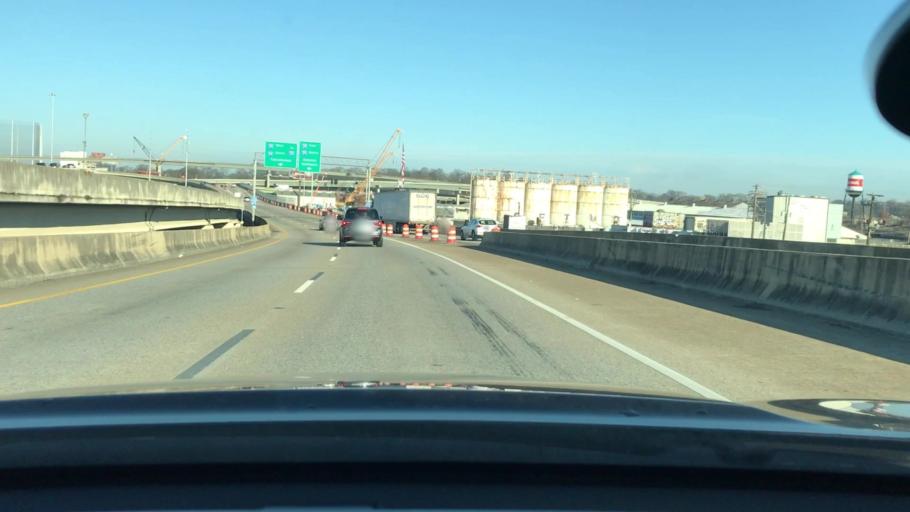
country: US
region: Alabama
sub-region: Jefferson County
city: Birmingham
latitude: 33.5242
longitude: -86.7999
